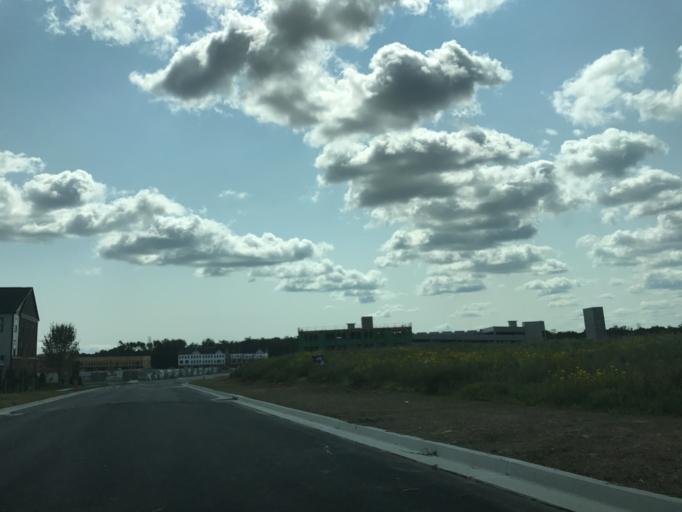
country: US
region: Maryland
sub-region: Baltimore County
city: Bowleys Quarters
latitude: 39.3616
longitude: -76.4029
